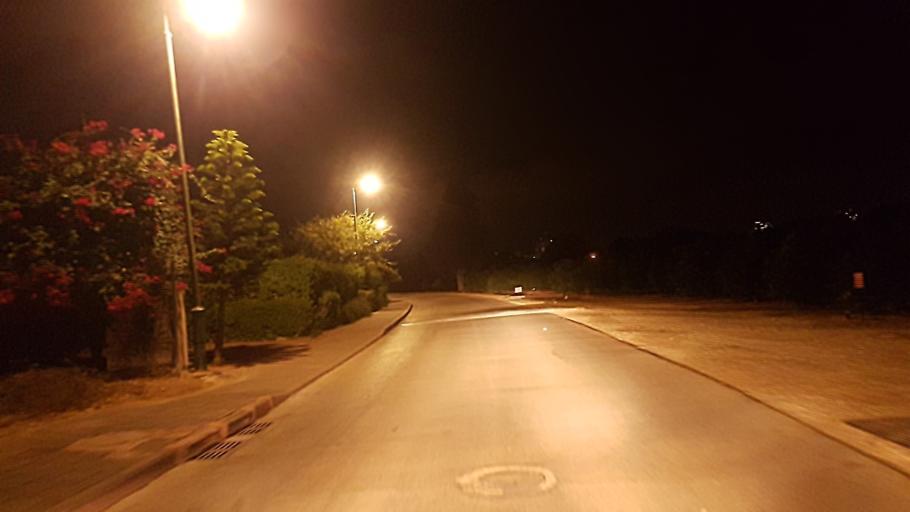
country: IL
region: Central District
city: Hod HaSharon
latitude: 32.1469
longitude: 34.9024
